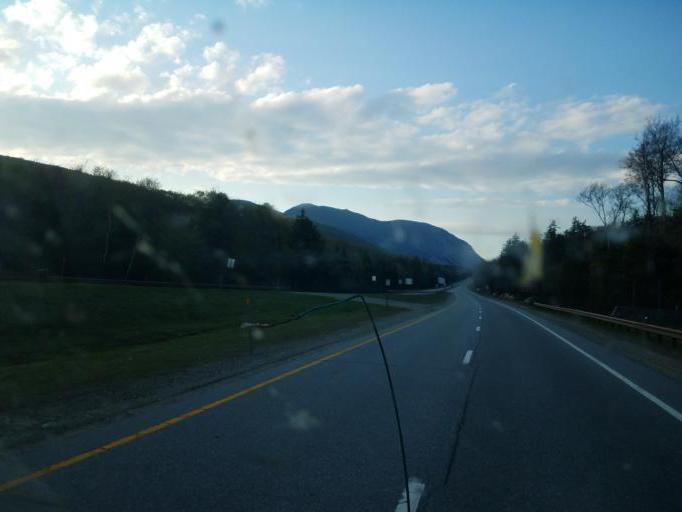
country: US
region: New Hampshire
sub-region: Grafton County
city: Woodstock
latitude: 44.1115
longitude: -71.6819
